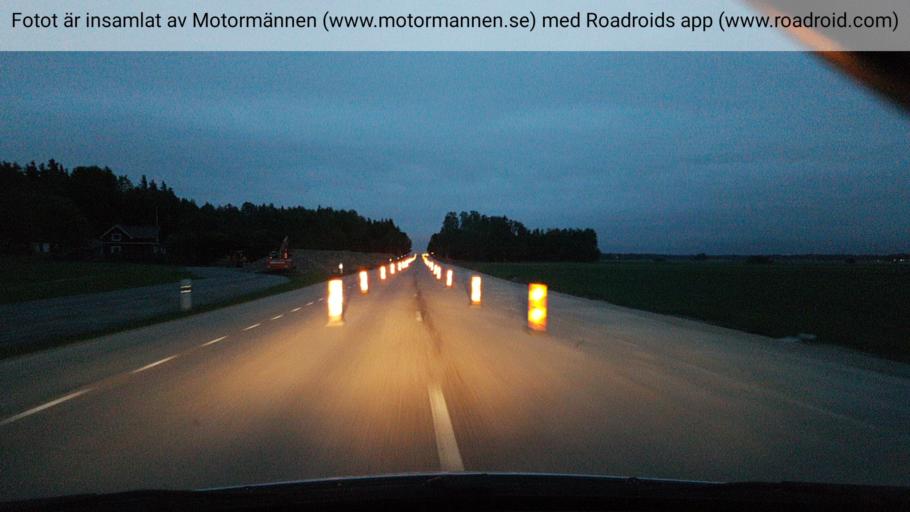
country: SE
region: Uppsala
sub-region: Enkopings Kommun
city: Irsta
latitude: 59.7142
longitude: 16.9750
